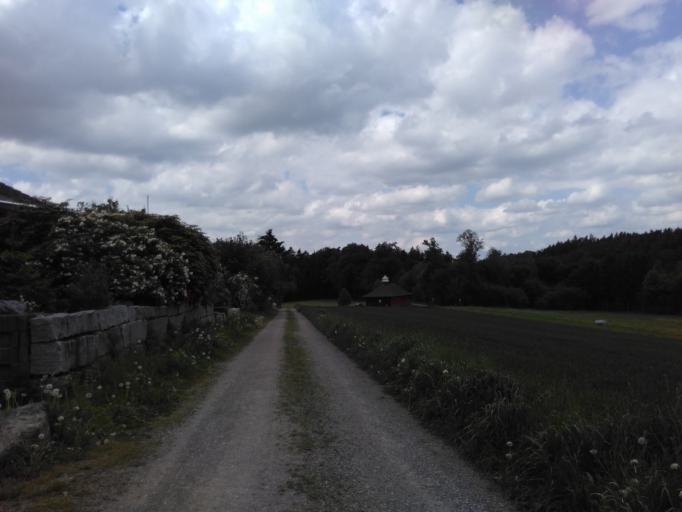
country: CH
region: Zurich
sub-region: Bezirk Hinwil
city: Wetzikon / Robenhausen
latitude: 47.3348
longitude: 8.7628
